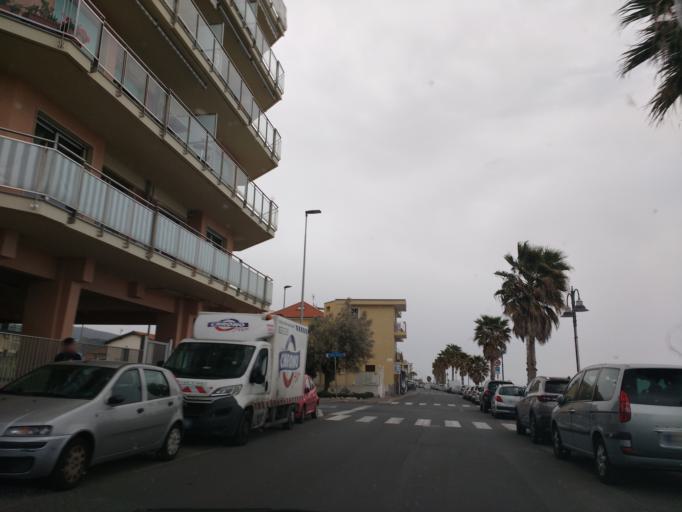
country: IT
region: Liguria
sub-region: Provincia di Imperia
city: Ventimiglia
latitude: 43.7857
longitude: 7.6198
